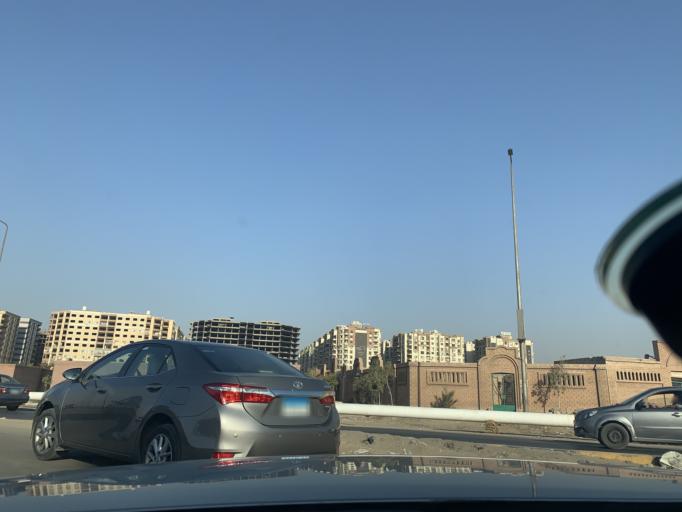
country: EG
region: Muhafazat al Qahirah
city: Cairo
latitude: 30.0328
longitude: 31.3520
